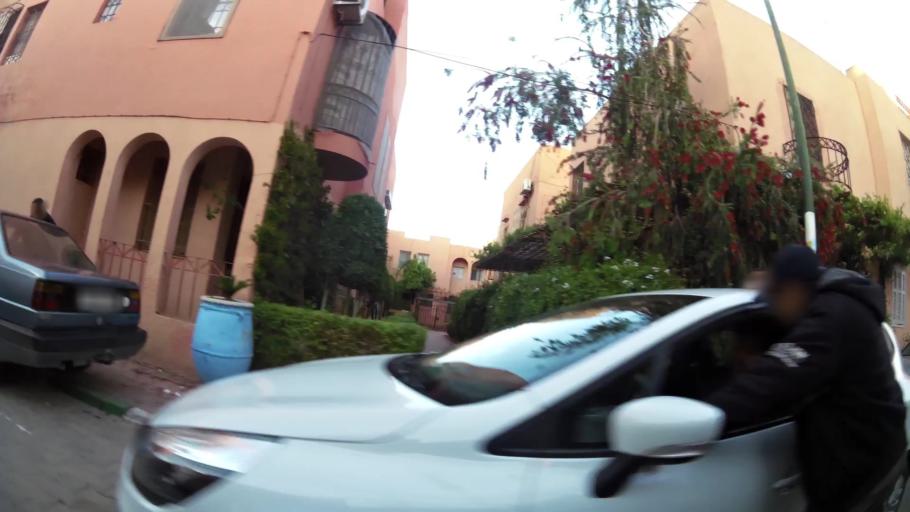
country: MA
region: Marrakech-Tensift-Al Haouz
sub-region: Marrakech
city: Marrakesh
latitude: 31.6394
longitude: -8.0390
